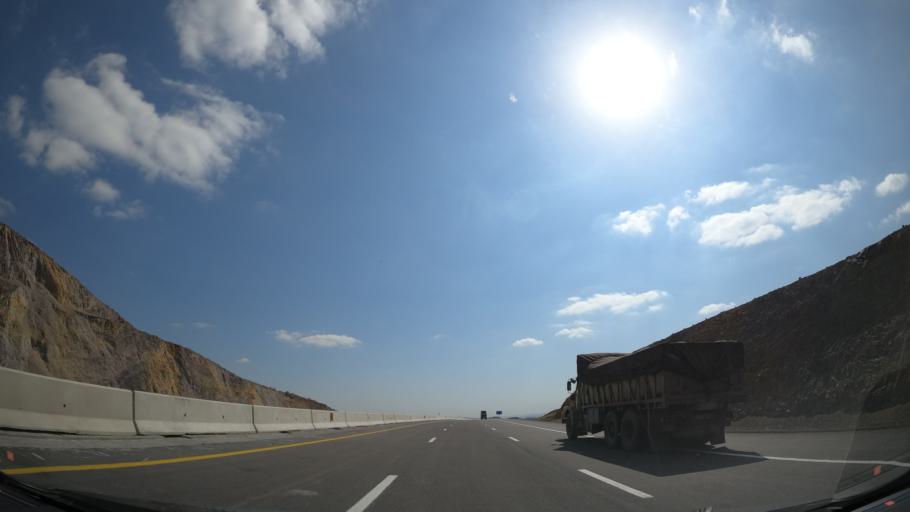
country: IR
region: Alborz
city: Nazarabad
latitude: 35.6806
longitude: 50.6426
